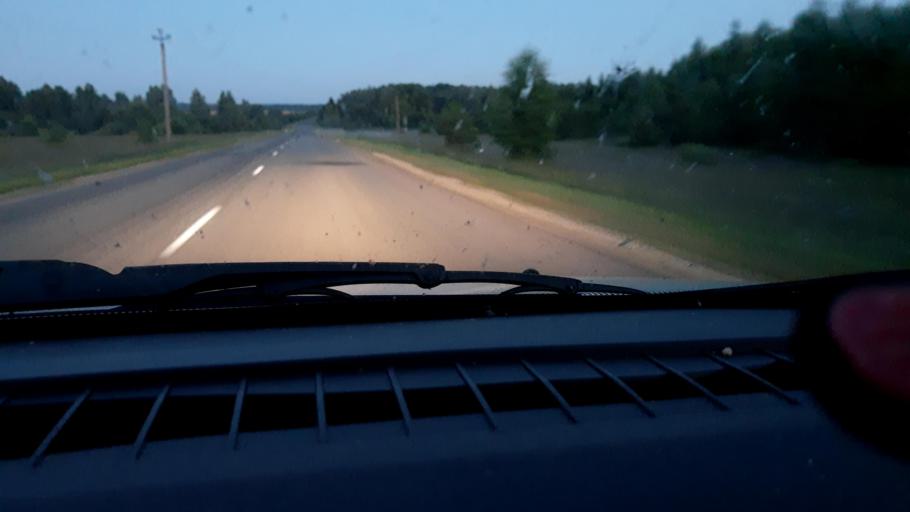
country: RU
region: Nizjnij Novgorod
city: Tonkino
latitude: 57.3696
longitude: 46.4214
